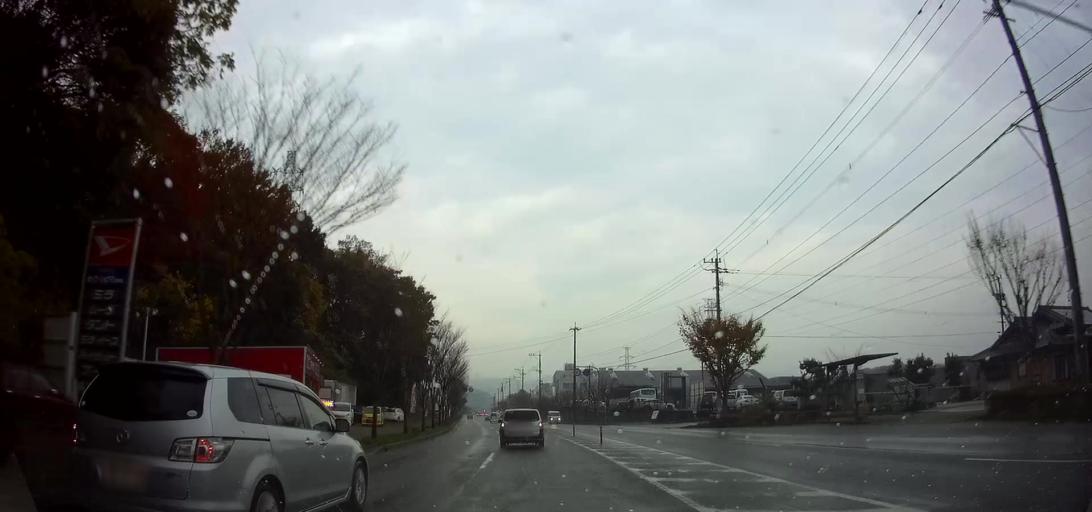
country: JP
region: Nagasaki
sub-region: Isahaya-shi
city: Isahaya
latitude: 32.8416
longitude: 130.0133
